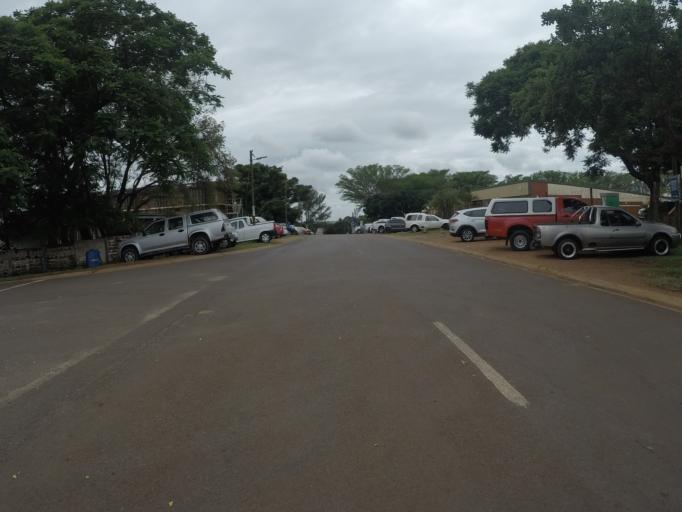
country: ZA
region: KwaZulu-Natal
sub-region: uThungulu District Municipality
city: Empangeni
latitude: -28.7747
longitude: 31.8621
